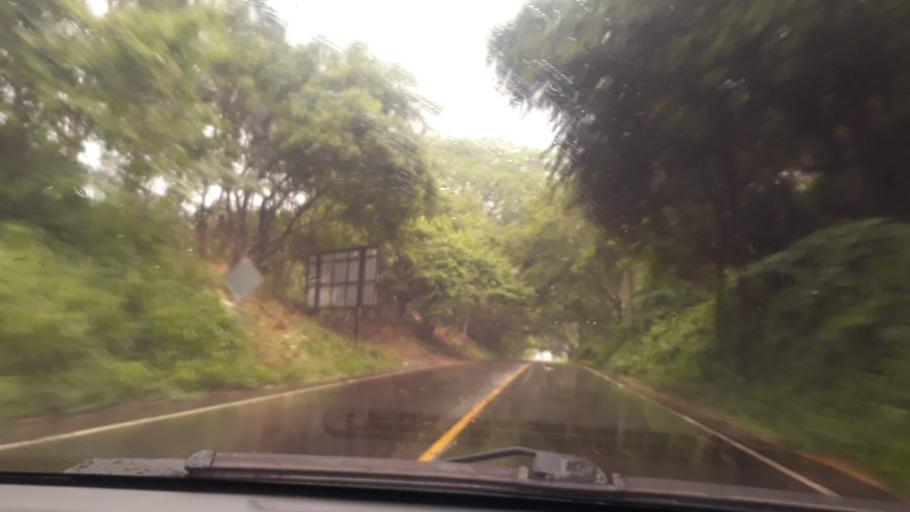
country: GT
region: Santa Rosa
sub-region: Municipio de Taxisco
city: Taxisco
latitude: 14.0791
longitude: -90.4849
